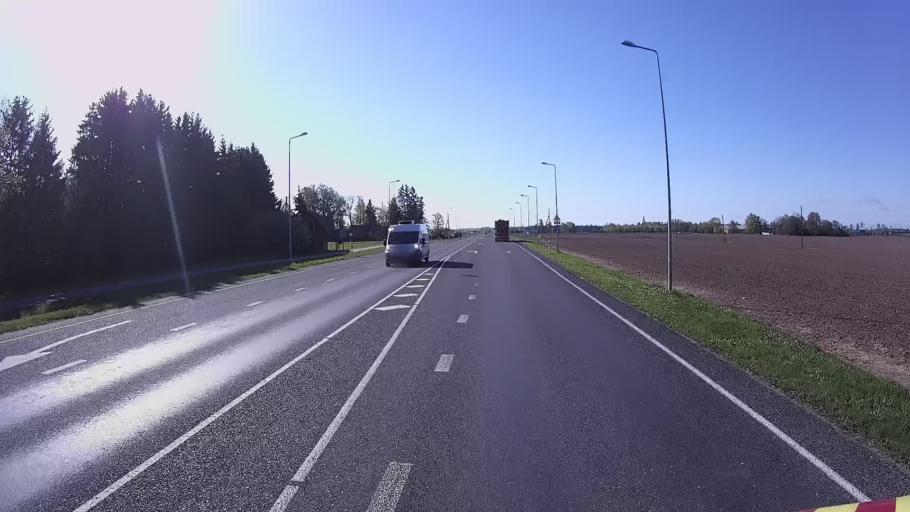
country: EE
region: Jaervamaa
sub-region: Paide linn
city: Paide
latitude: 58.7573
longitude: 25.5580
